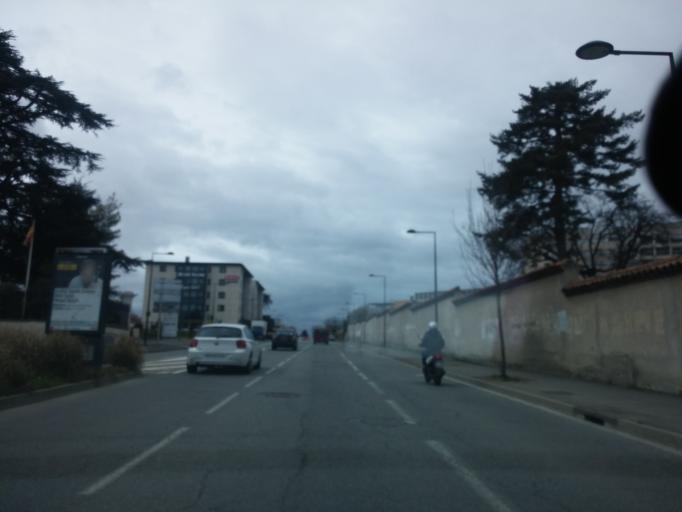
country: FR
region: Midi-Pyrenees
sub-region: Departement de la Haute-Garonne
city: Blagnac
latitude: 43.6063
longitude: 1.4013
